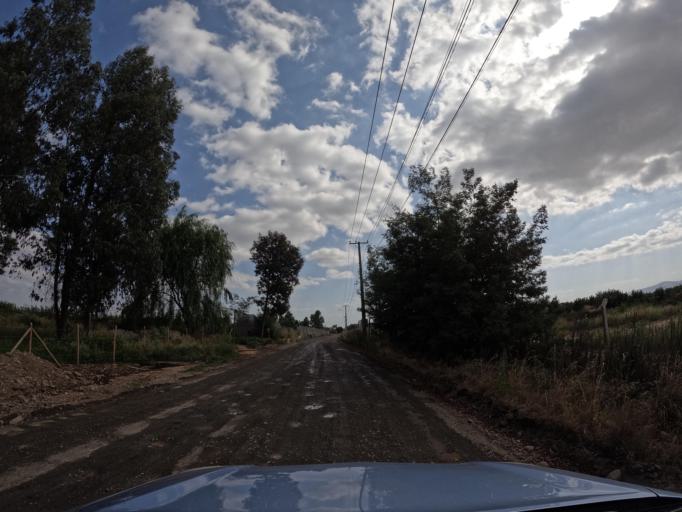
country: CL
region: Maule
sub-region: Provincia de Curico
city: Molina
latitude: -35.1673
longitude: -71.2907
